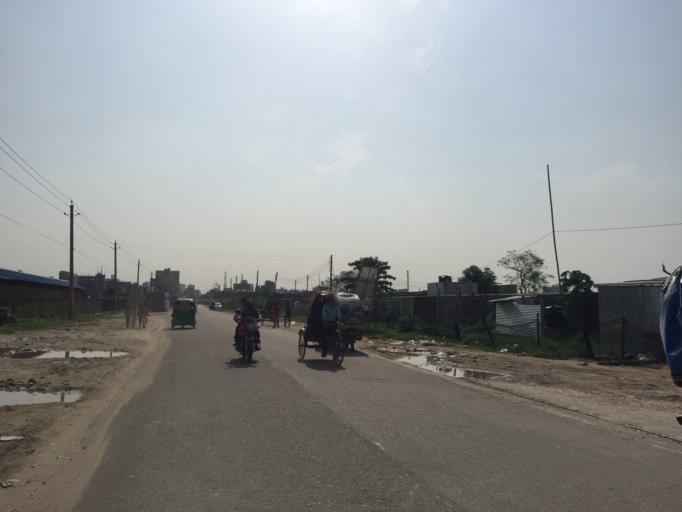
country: BD
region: Dhaka
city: Paltan
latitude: 23.7996
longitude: 90.4435
